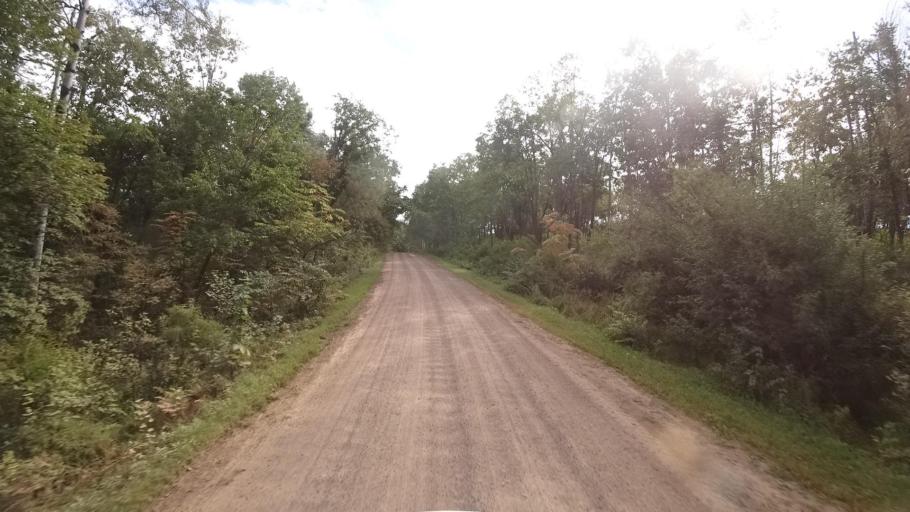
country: RU
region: Primorskiy
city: Dostoyevka
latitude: 44.3542
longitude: 133.5213
